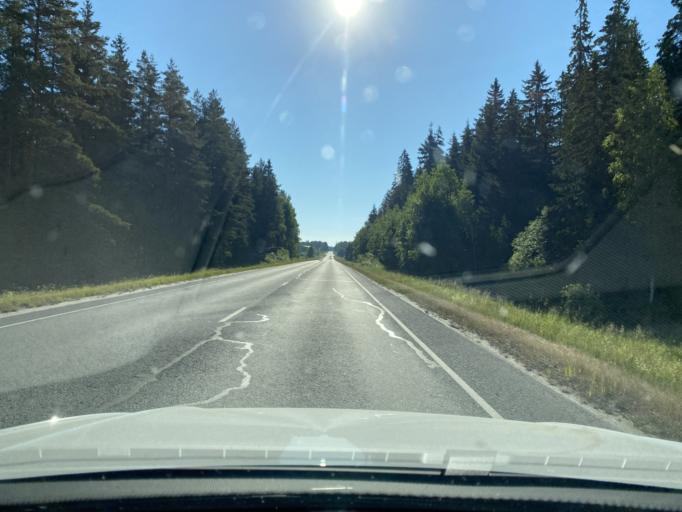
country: FI
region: Haeme
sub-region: Forssa
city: Forssa
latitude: 60.8297
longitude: 23.6780
